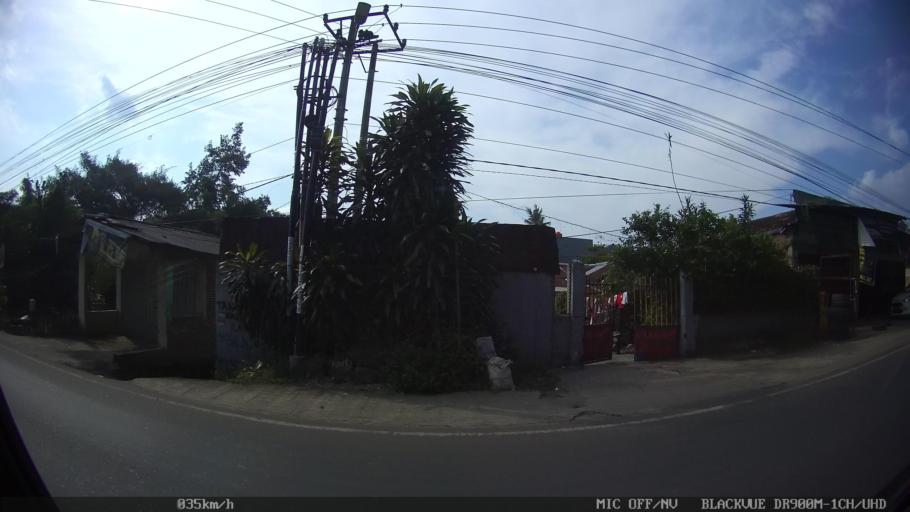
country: ID
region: Lampung
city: Kedaton
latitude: -5.3934
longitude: 105.2228
